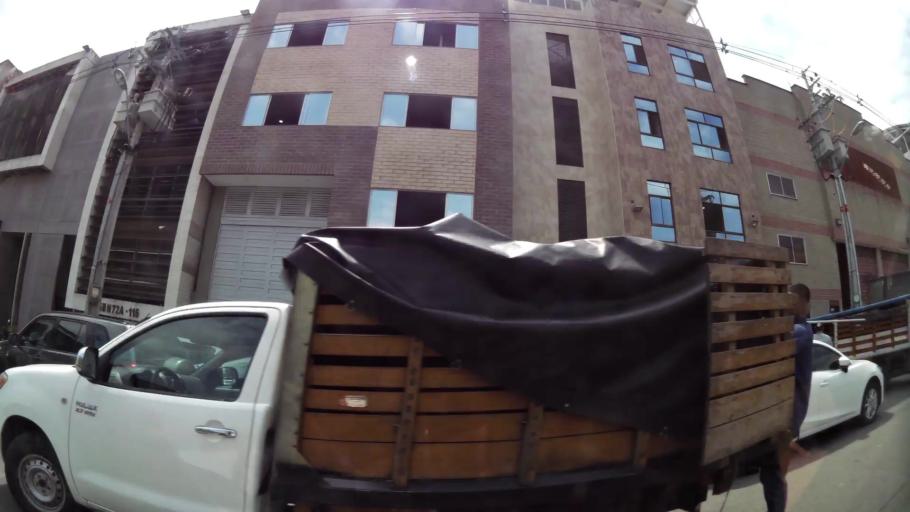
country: CO
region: Antioquia
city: Itagui
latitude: 6.1871
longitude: -75.6002
